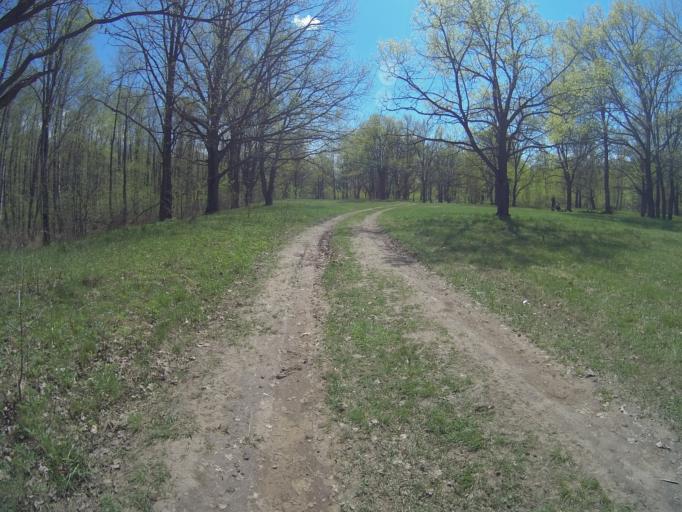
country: RU
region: Vladimir
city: Kommunar
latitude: 56.0979
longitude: 40.4315
